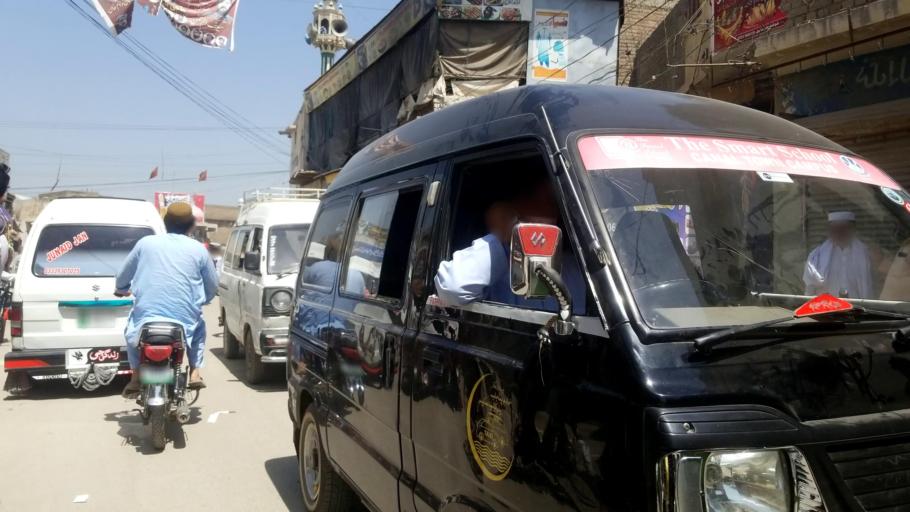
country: PK
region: Khyber Pakhtunkhwa
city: Peshawar
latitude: 34.0278
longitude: 71.4885
